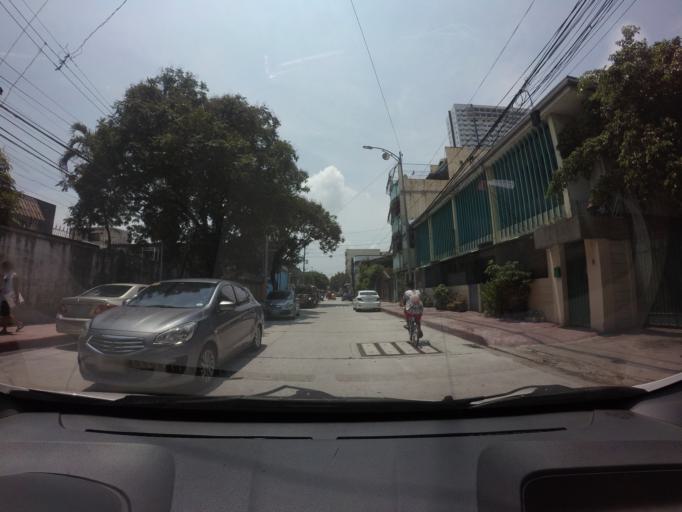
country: PH
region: Metro Manila
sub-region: City of Manila
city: Quiapo
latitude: 14.5821
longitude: 120.9949
